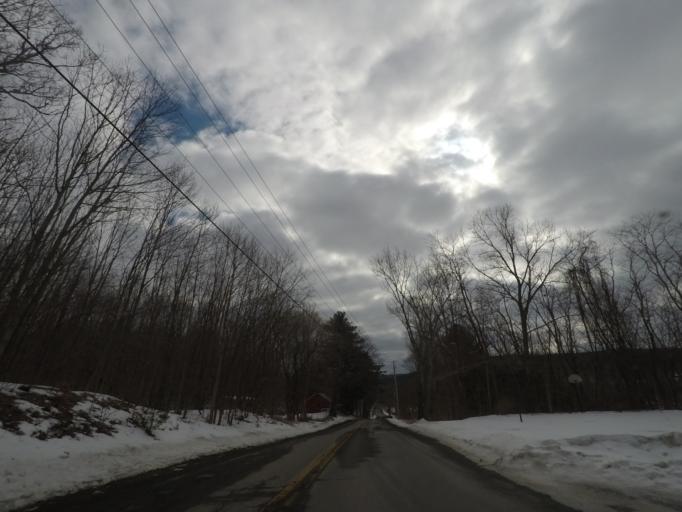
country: US
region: New York
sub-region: Rensselaer County
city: Hoosick Falls
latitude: 42.9034
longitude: -73.4260
